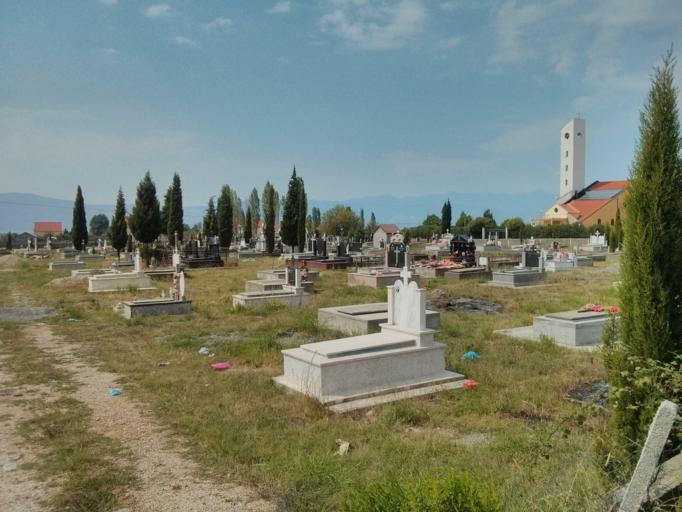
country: AL
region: Shkoder
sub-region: Rrethi i Malesia e Madhe
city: Grude-Fushe
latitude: 42.1432
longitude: 19.5034
